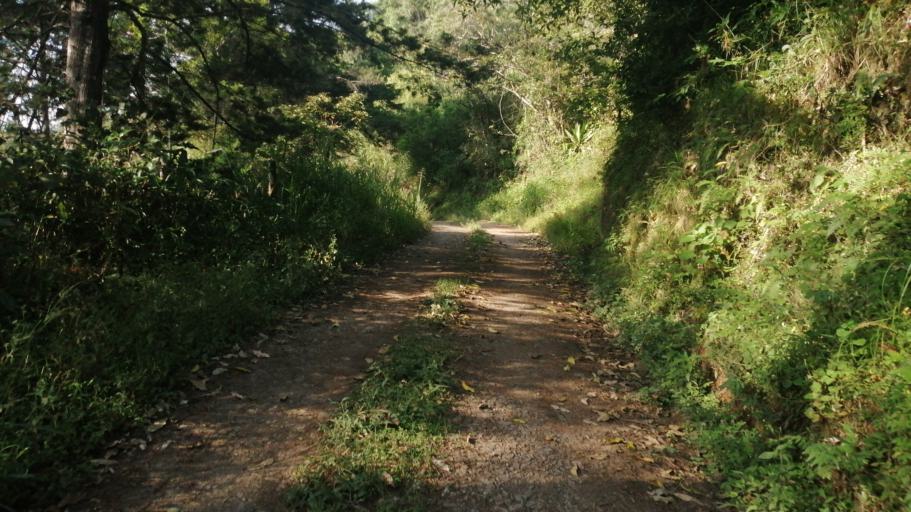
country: CO
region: Boyaca
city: Garagoa
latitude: 5.0784
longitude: -73.3887
